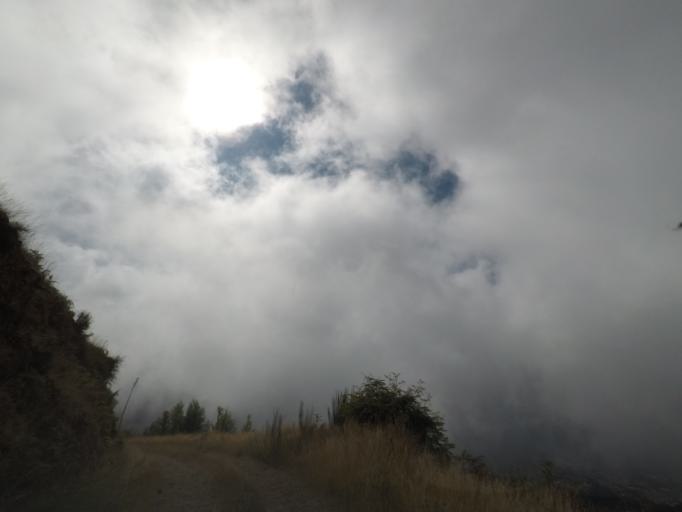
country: PT
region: Madeira
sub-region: Funchal
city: Nossa Senhora do Monte
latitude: 32.6991
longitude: -16.9152
